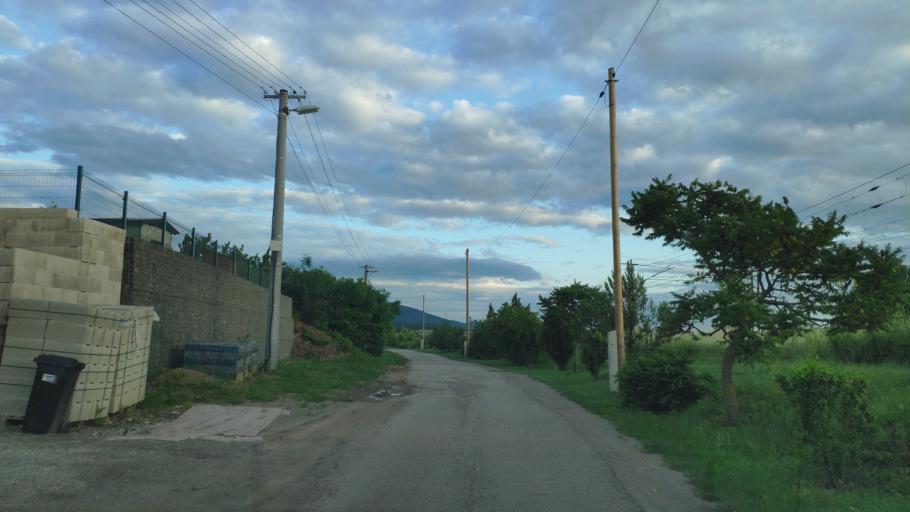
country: SK
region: Kosicky
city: Kosice
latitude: 48.6358
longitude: 21.3821
